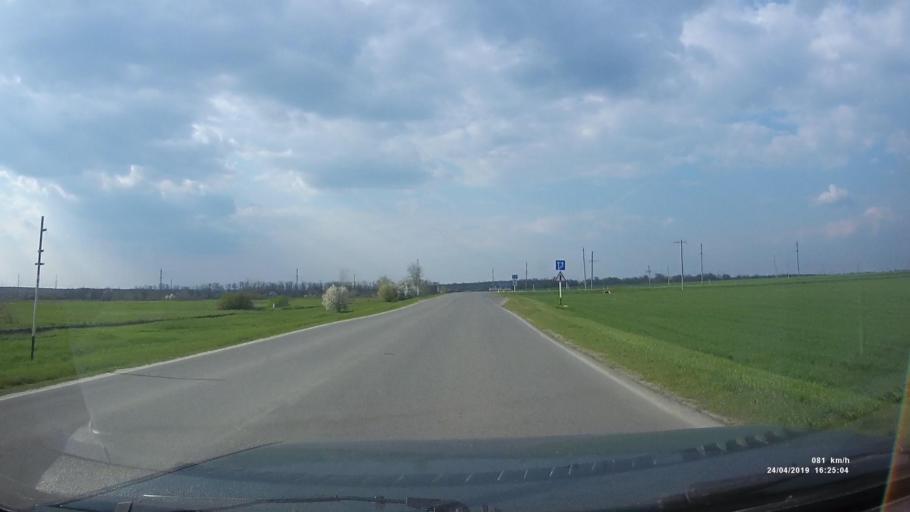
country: RU
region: Rostov
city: Orlovskiy
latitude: 46.8485
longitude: 42.0440
